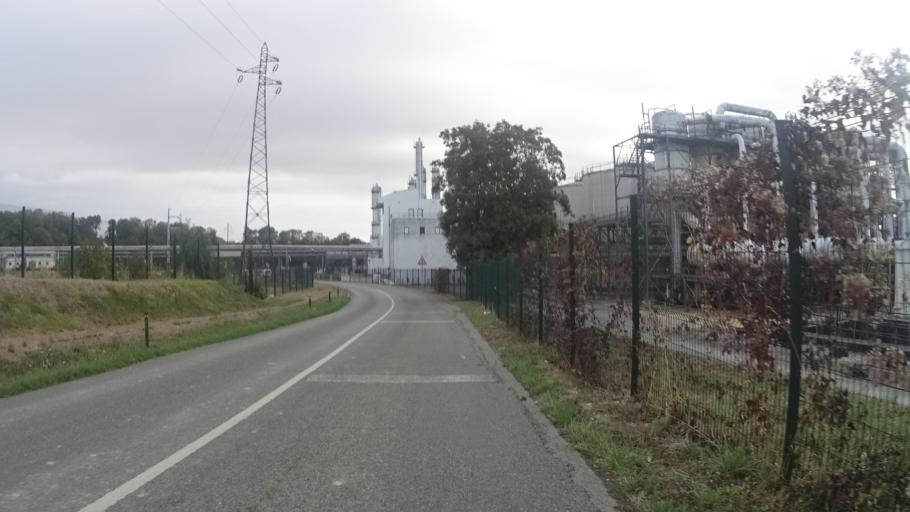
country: FR
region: Picardie
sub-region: Departement de l'Aisne
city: Origny-Sainte-Benoite
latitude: 49.8363
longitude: 3.4748
